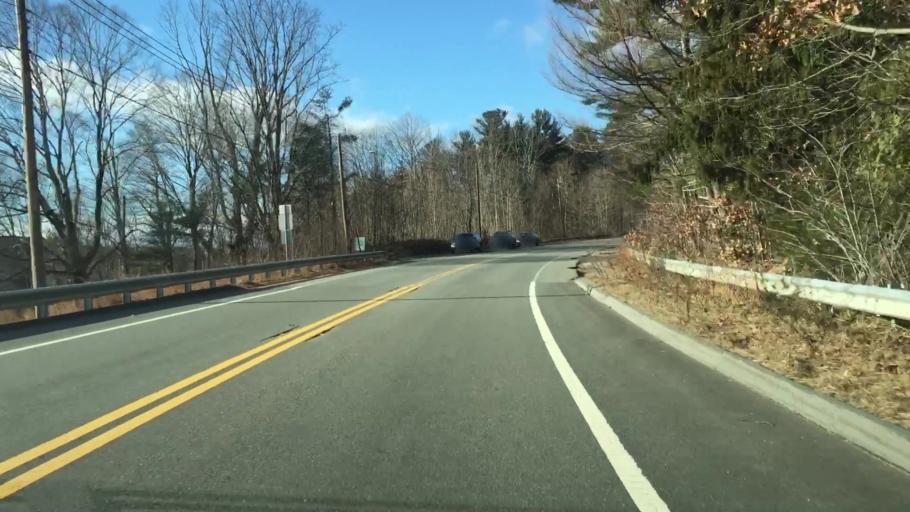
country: US
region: Massachusetts
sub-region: Worcester County
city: West Boylston
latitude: 42.3760
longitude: -71.7811
